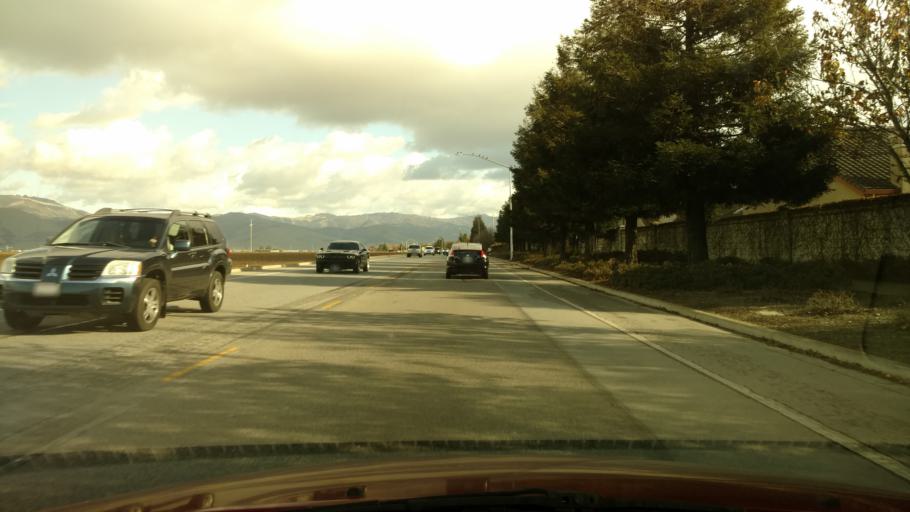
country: US
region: California
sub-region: Monterey County
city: Boronda
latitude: 36.7166
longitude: -121.6405
